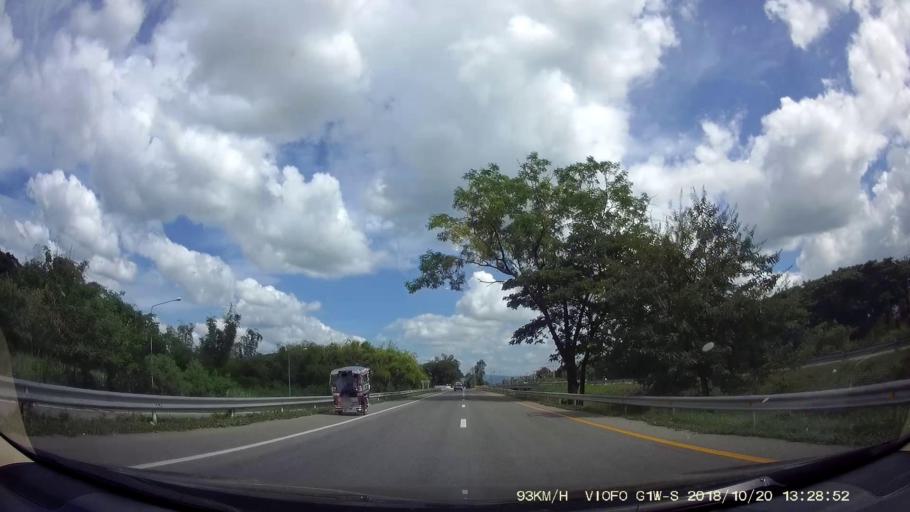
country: TH
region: Chaiyaphum
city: Khon San
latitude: 16.5909
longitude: 101.9817
